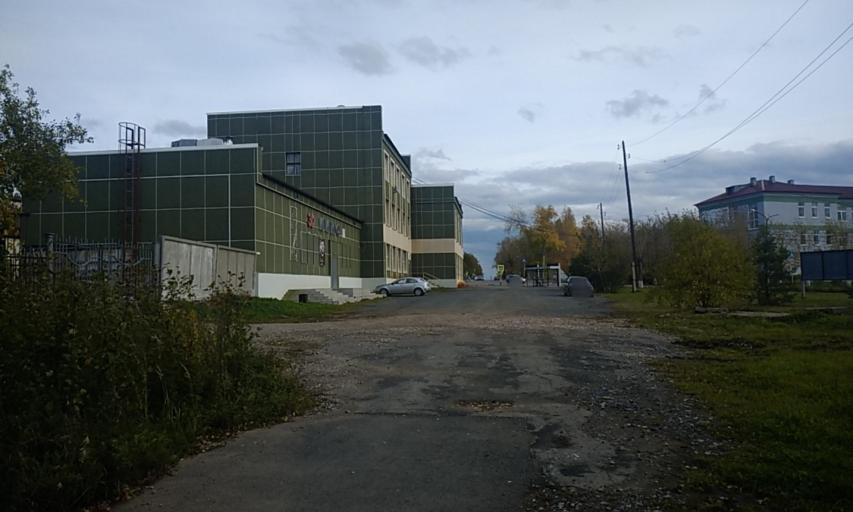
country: RU
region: Sverdlovsk
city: Krasnoural'sk
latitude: 58.3543
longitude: 60.0537
